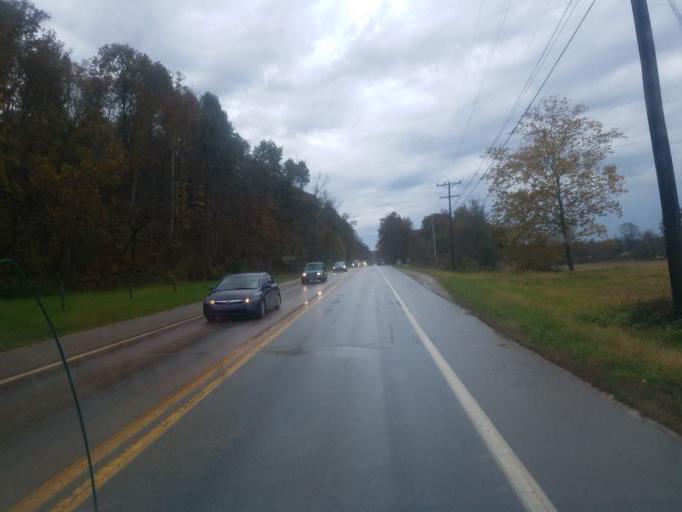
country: US
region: West Virginia
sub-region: Wood County
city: Williamstown
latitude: 39.3858
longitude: -81.4742
